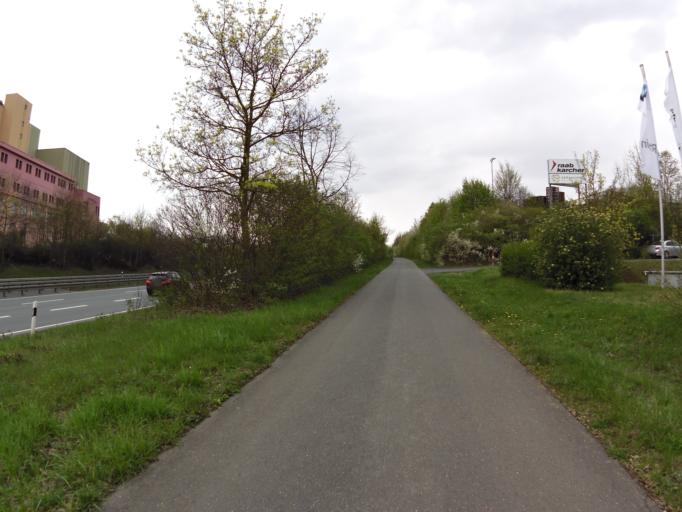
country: DE
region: Bavaria
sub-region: Regierungsbezirk Unterfranken
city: Gerbrunn
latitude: 49.7930
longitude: 9.9959
